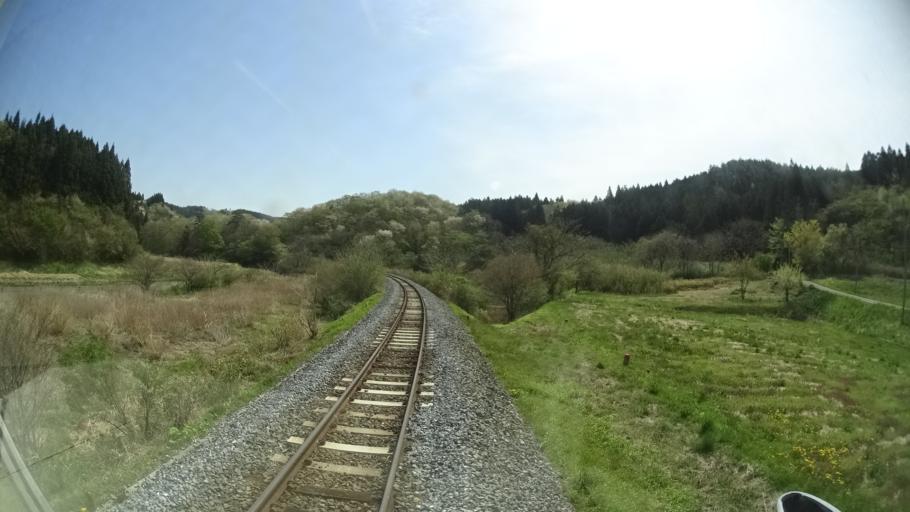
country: JP
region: Iwate
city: Ofunato
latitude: 38.9136
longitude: 141.4938
